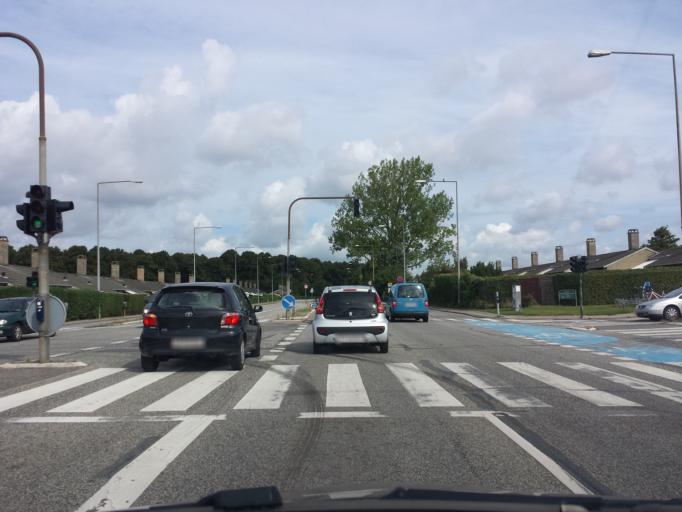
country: DK
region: Capital Region
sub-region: Rodovre Kommune
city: Rodovre
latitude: 55.6955
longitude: 12.4488
